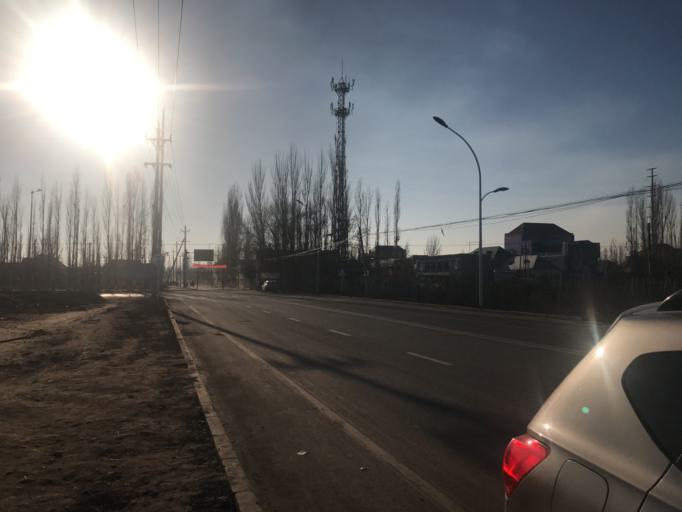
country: CN
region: Xinjiang Uygur Zizhiqu
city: Yengiyar
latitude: 43.9409
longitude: 81.2178
